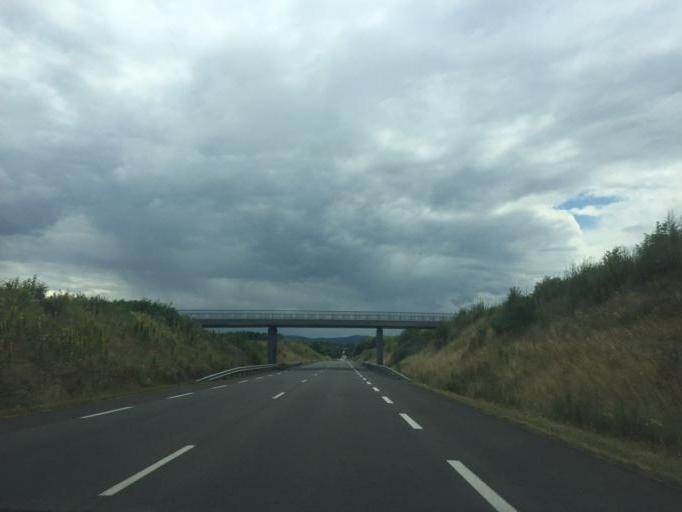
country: FR
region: Rhone-Alpes
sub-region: Departement de l'Isere
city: Janneyrias
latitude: 45.7595
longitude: 5.1279
